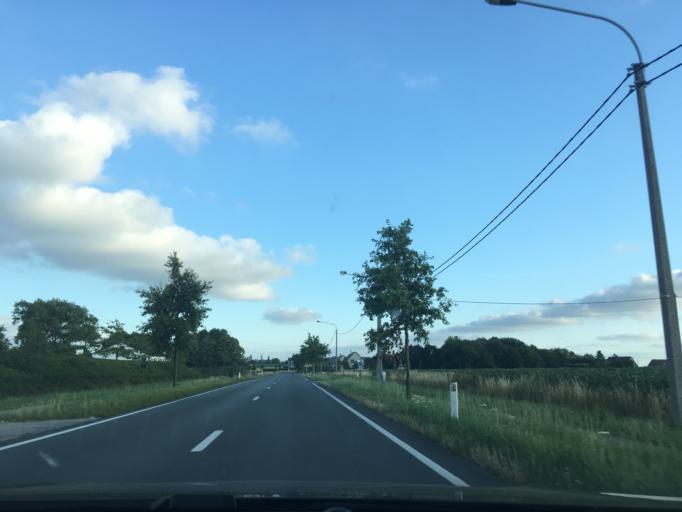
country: BE
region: Flanders
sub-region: Provincie West-Vlaanderen
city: Tielt
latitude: 51.0199
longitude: 3.3093
